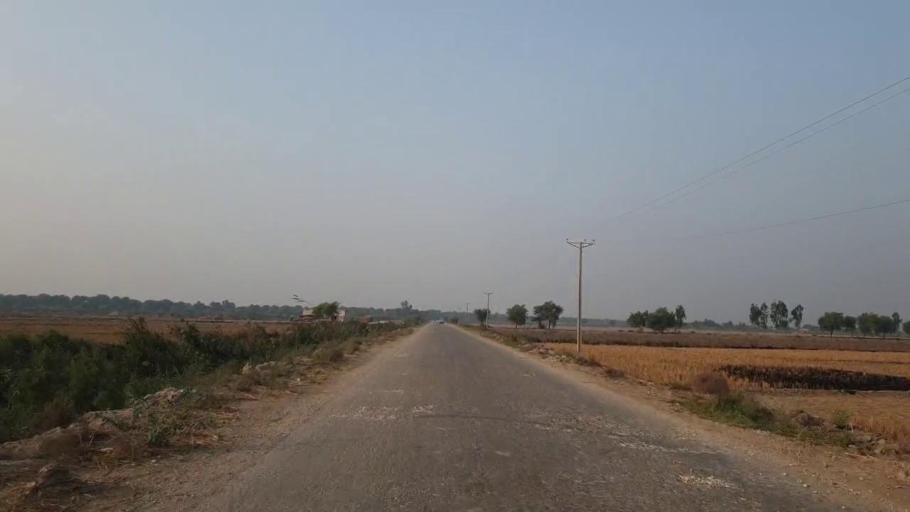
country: PK
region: Sindh
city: Tando Muhammad Khan
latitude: 25.1088
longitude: 68.4295
